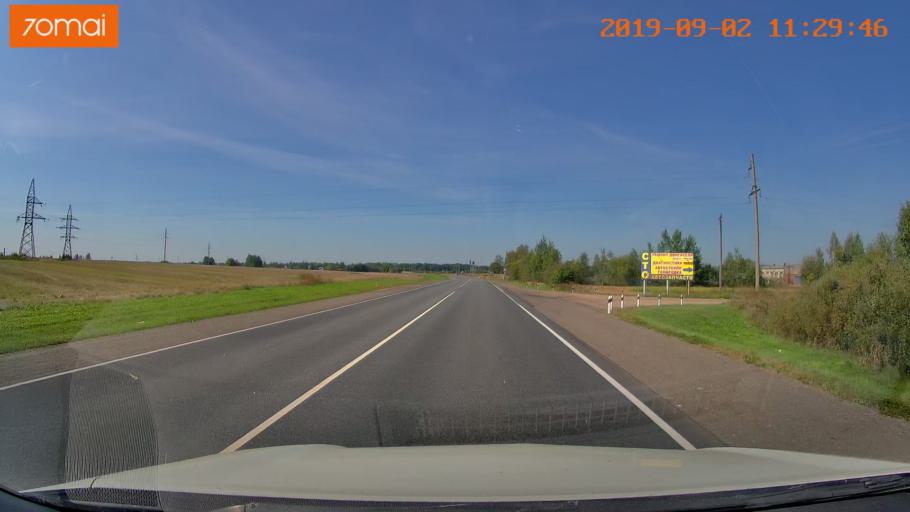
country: RU
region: Smolensk
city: Roslavl'
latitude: 53.9882
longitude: 32.8513
